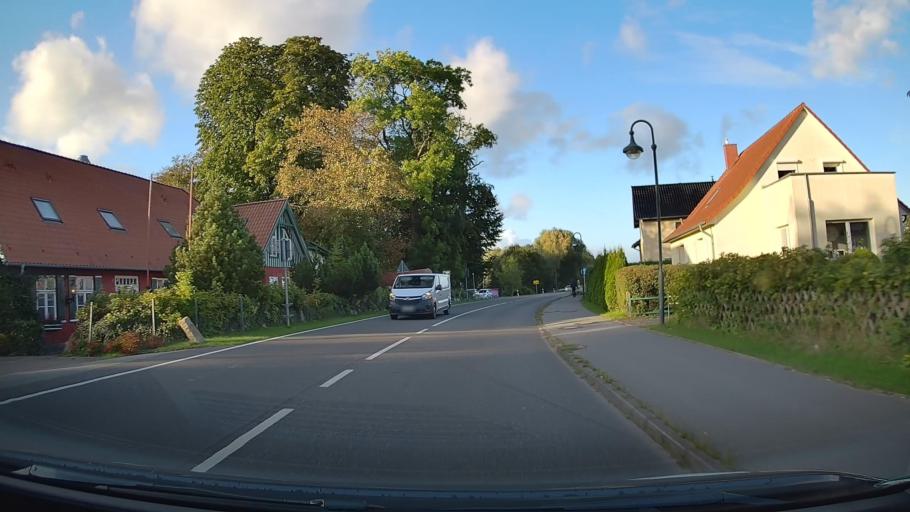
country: DE
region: Mecklenburg-Vorpommern
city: Wendorf
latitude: 54.2612
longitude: 13.0302
